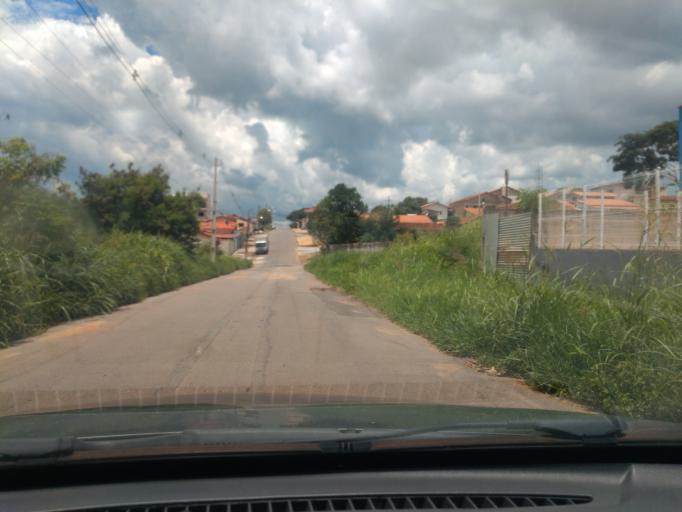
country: BR
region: Minas Gerais
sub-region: Tres Coracoes
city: Tres Coracoes
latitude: -21.6793
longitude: -45.2723
